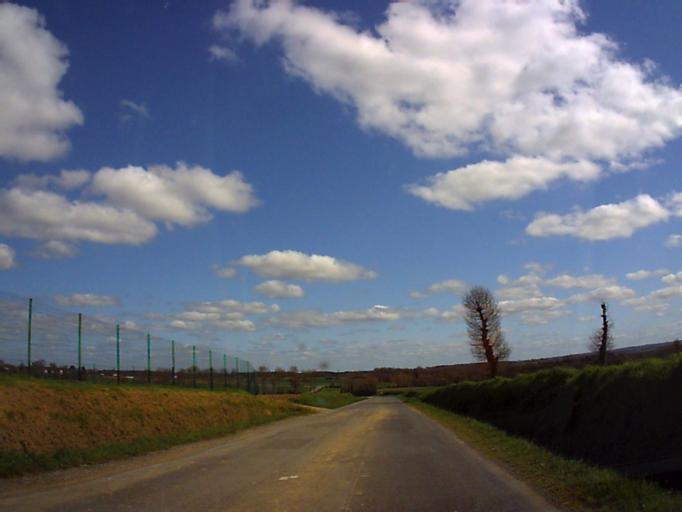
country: FR
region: Brittany
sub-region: Departement d'Ille-et-Vilaine
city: Saint-Meen-le-Grand
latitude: 48.1751
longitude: -2.1705
